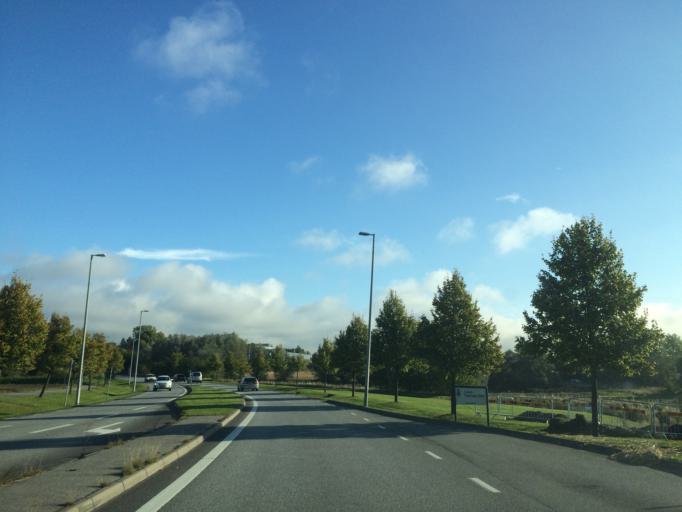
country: SE
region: Skane
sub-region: Lunds Kommun
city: Lund
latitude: 55.6804
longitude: 13.1834
